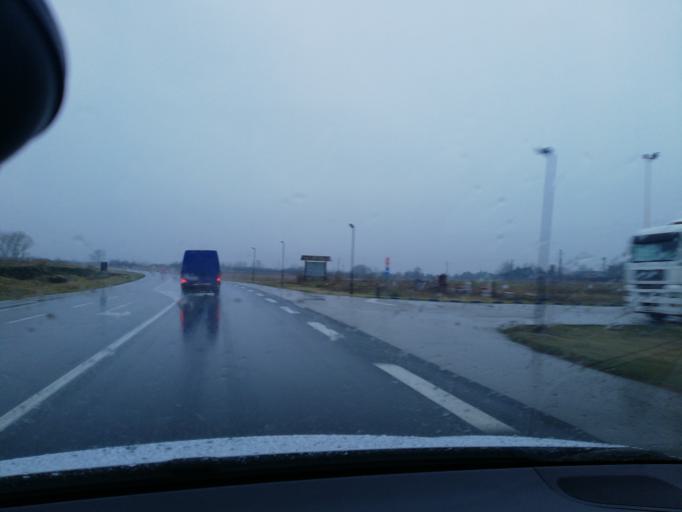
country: RS
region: Autonomna Pokrajina Vojvodina
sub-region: Sremski Okrug
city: Ruma
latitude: 45.0247
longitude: 19.8347
